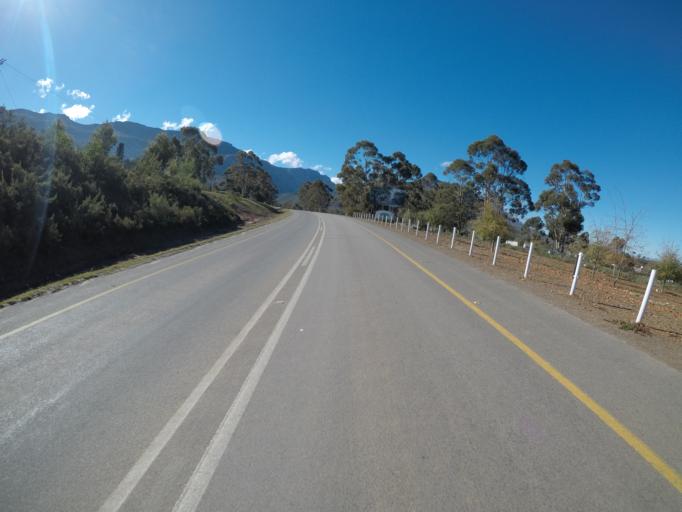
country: ZA
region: Western Cape
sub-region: Overberg District Municipality
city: Caledon
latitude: -34.0556
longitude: 19.6009
